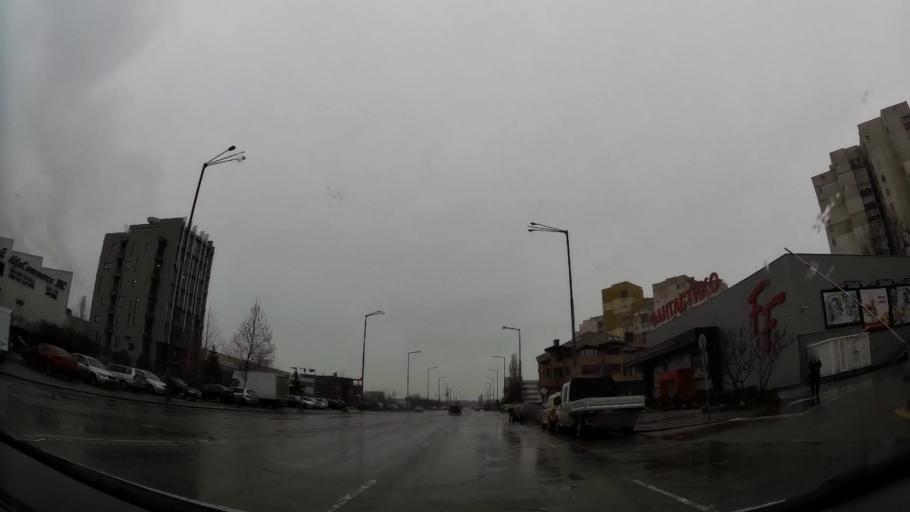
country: BG
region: Sofia-Capital
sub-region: Stolichna Obshtina
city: Sofia
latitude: 42.6502
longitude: 23.4073
